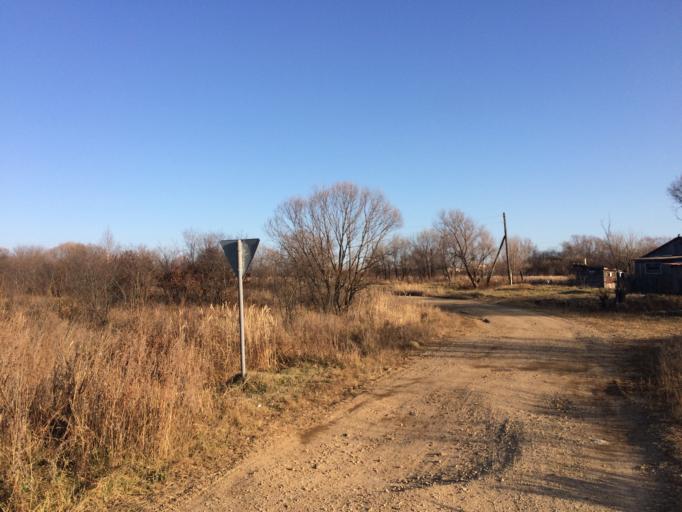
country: RU
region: Primorskiy
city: Ivanovka
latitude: 43.9547
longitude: 132.4636
